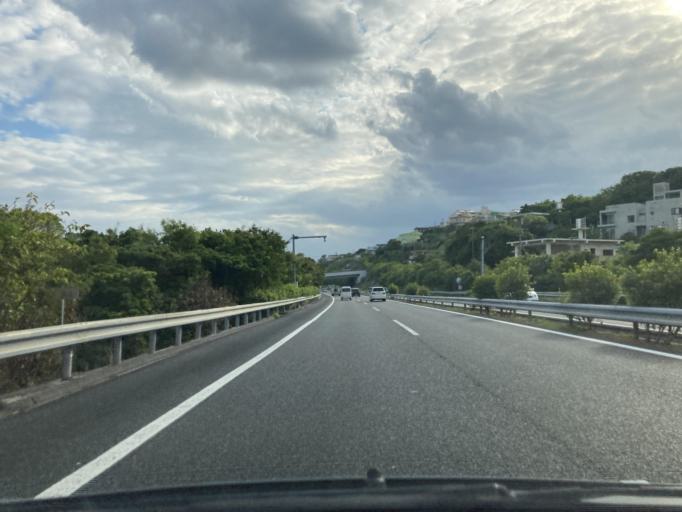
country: JP
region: Okinawa
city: Ginowan
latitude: 26.2706
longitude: 127.7765
